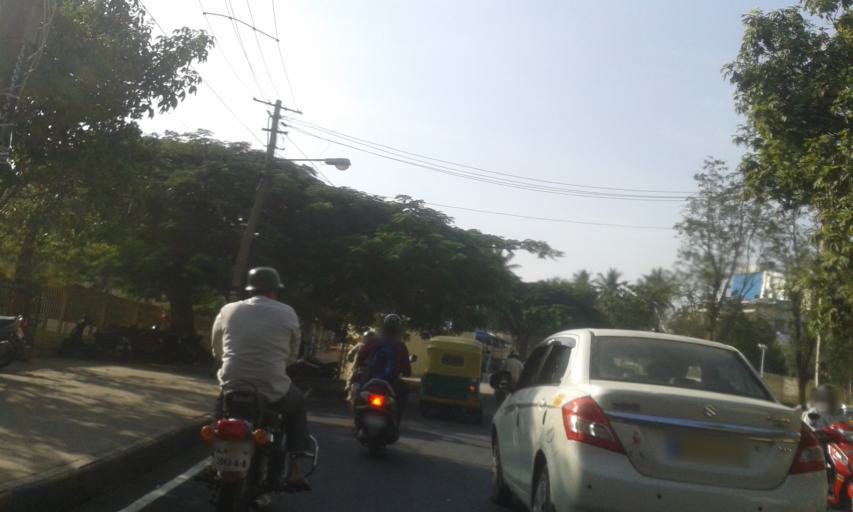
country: IN
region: Karnataka
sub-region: Bangalore Urban
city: Bangalore
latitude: 12.9349
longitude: 77.5860
